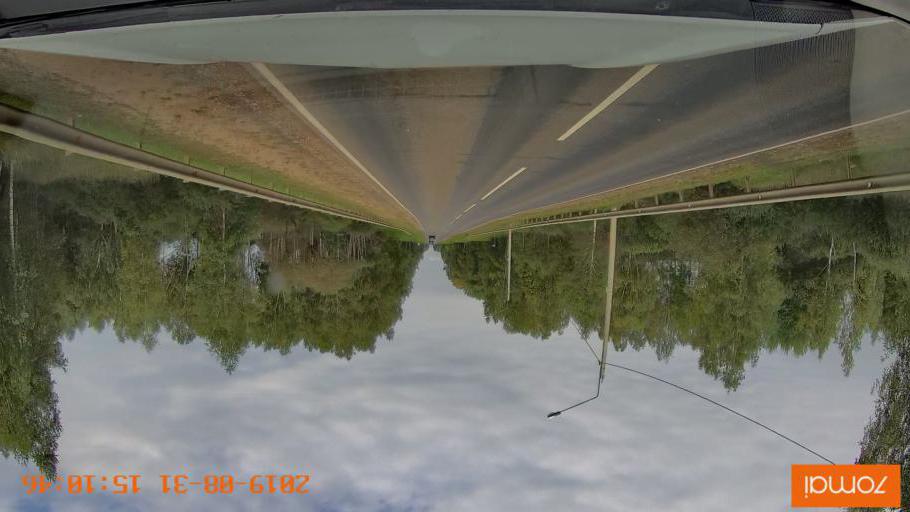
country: RU
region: Kaluga
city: Spas-Demensk
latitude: 54.4169
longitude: 34.2275
